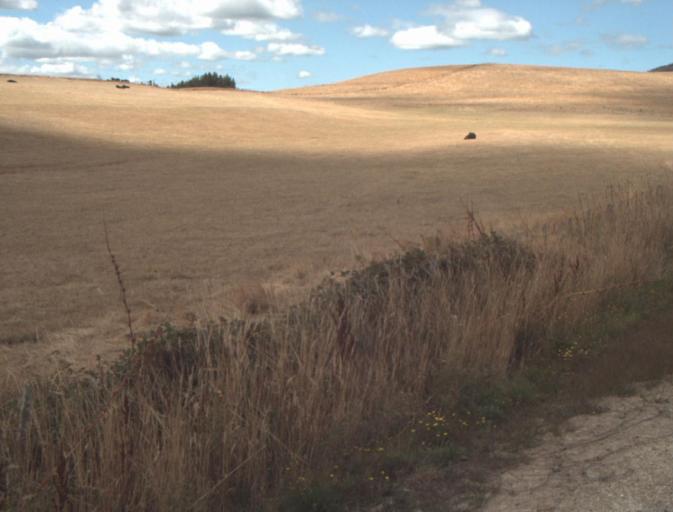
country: AU
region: Tasmania
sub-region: Launceston
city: Mayfield
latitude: -41.2111
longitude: 147.1088
